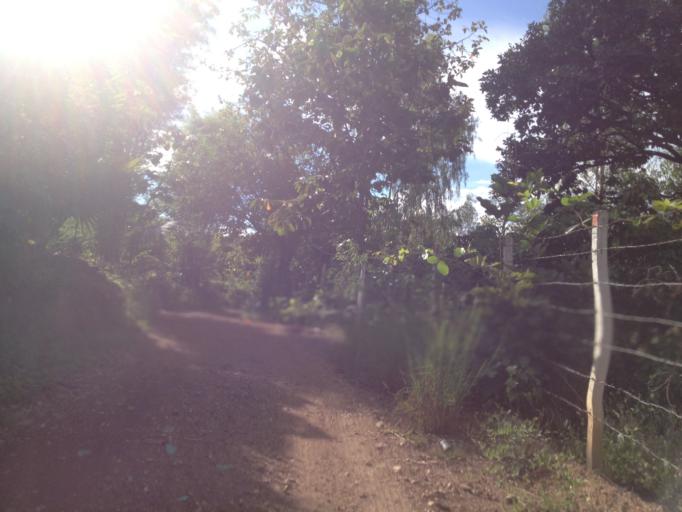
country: TH
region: Chiang Mai
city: Hang Dong
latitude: 18.7030
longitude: 98.8911
